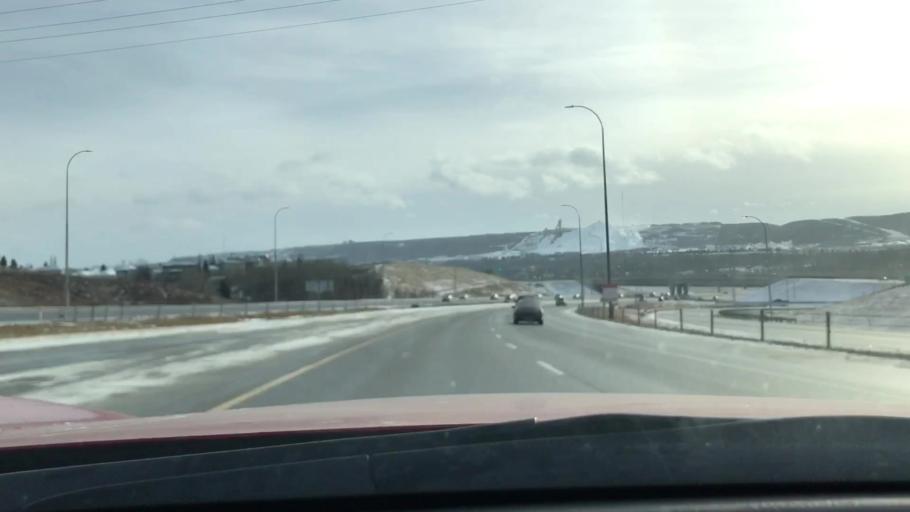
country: CA
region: Alberta
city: Calgary
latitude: 51.1110
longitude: -114.2249
